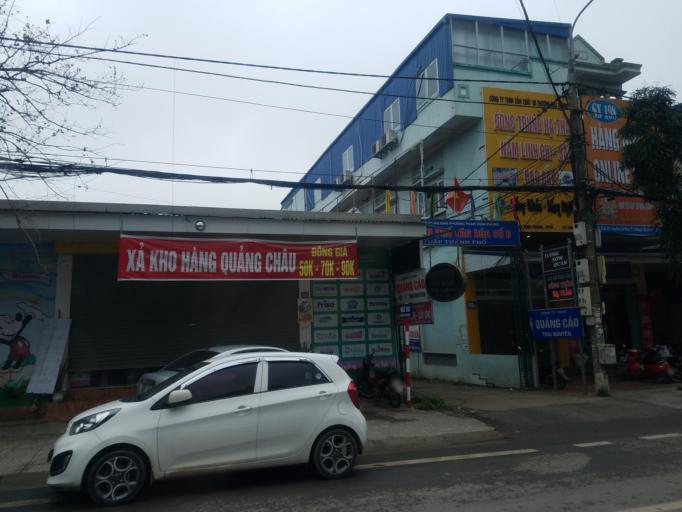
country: VN
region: Thai Nguyen
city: Thanh Pho Thai Nguyen
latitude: 21.5883
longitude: 105.8428
